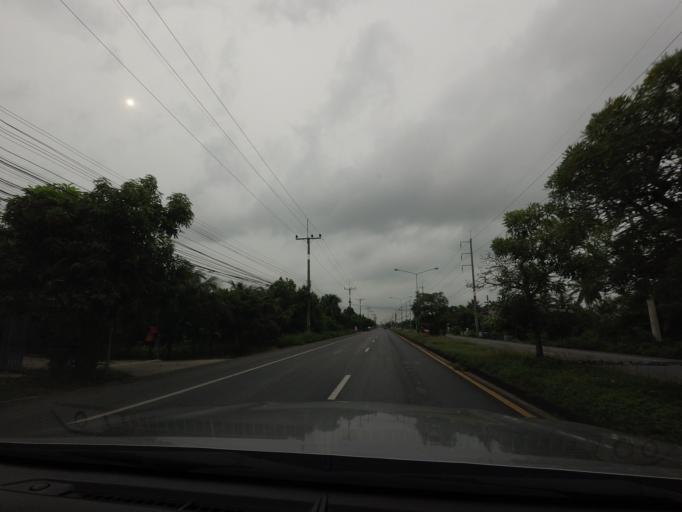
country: TH
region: Songkhla
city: Sathing Phra
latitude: 7.3798
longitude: 100.4734
